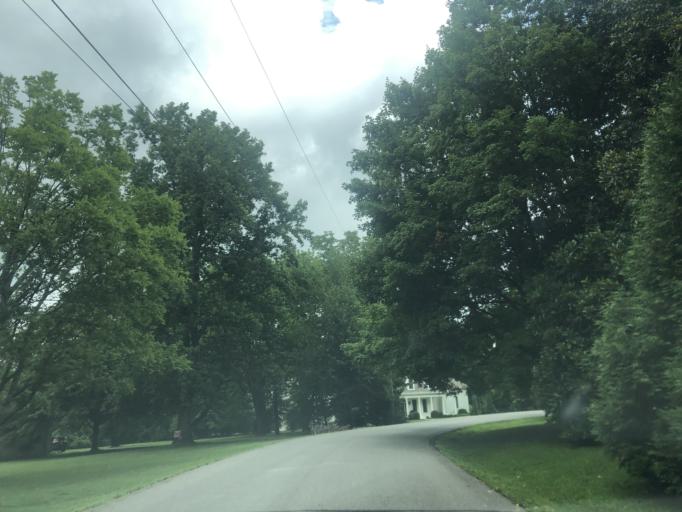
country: US
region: Tennessee
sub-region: Davidson County
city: Oak Hill
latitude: 36.0839
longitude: -86.7948
